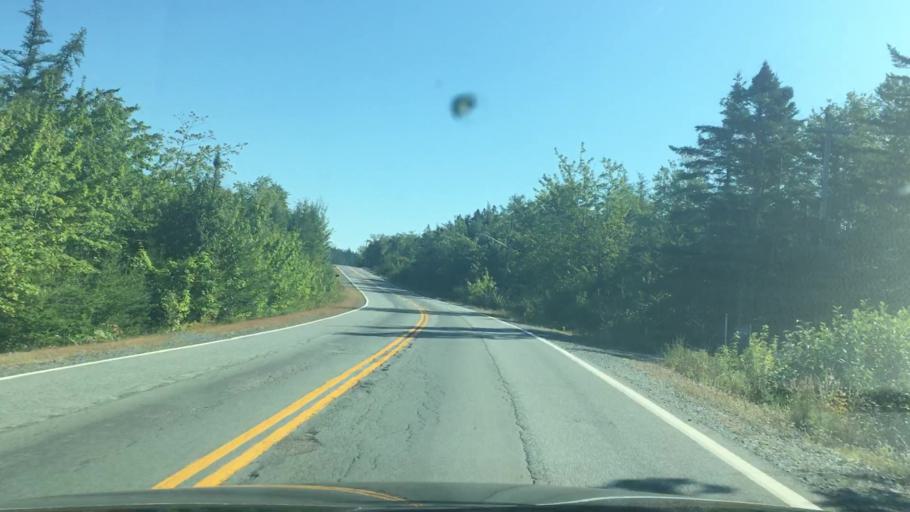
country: CA
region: Nova Scotia
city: Cole Harbour
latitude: 44.7758
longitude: -63.0491
